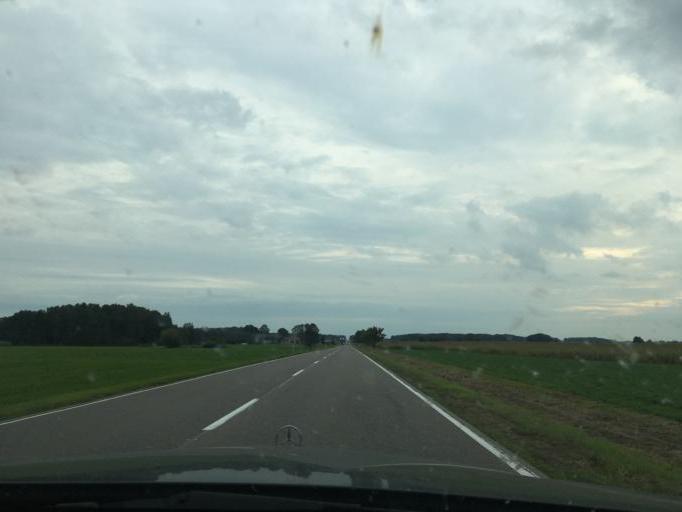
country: PL
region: Podlasie
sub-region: Powiat lomzynski
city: Sniadowo
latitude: 52.9814
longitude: 21.9008
